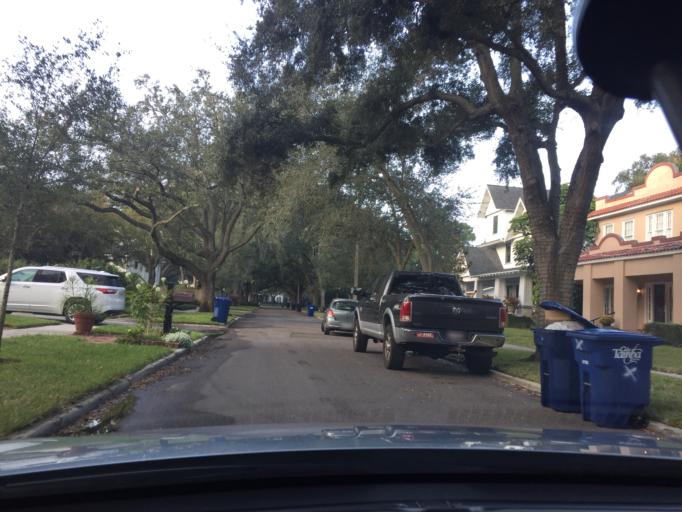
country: US
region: Florida
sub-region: Hillsborough County
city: Tampa
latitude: 27.9355
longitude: -82.4868
